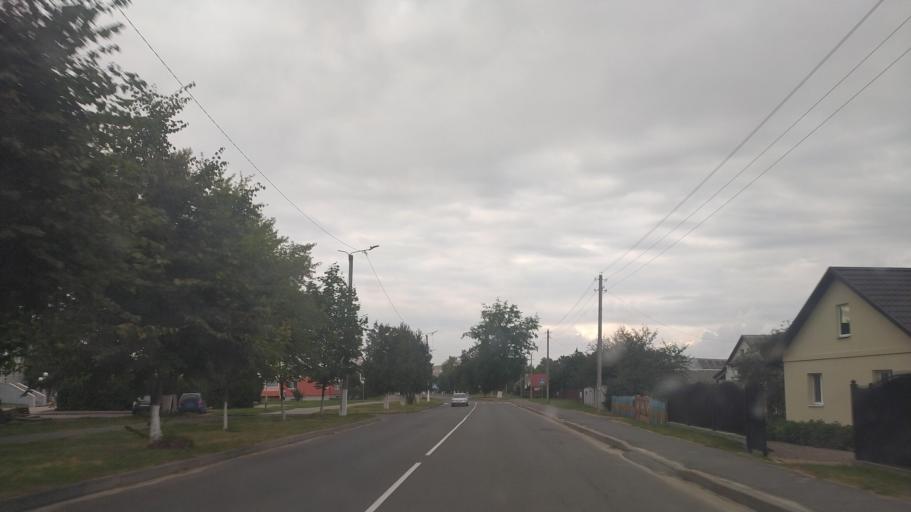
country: BY
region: Brest
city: Byaroza
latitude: 52.5296
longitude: 24.9873
